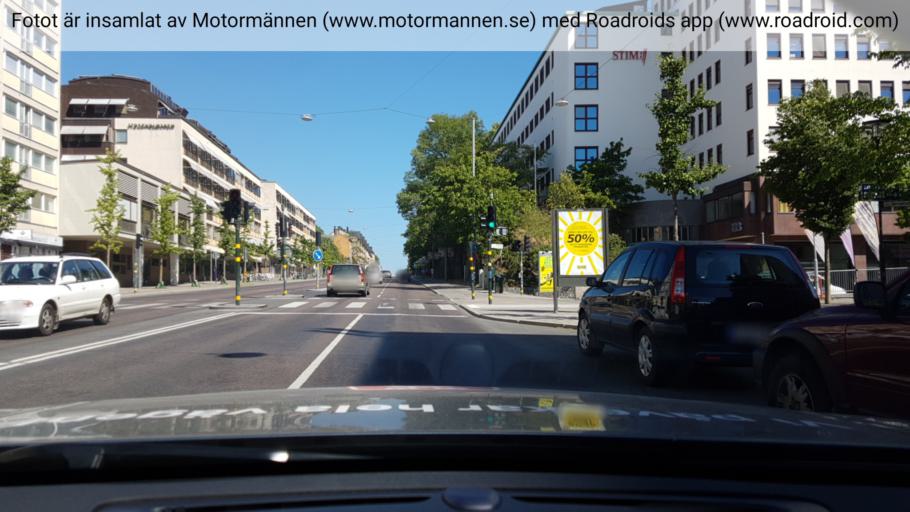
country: SE
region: Stockholm
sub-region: Stockholms Kommun
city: Arsta
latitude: 59.3161
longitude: 18.0422
